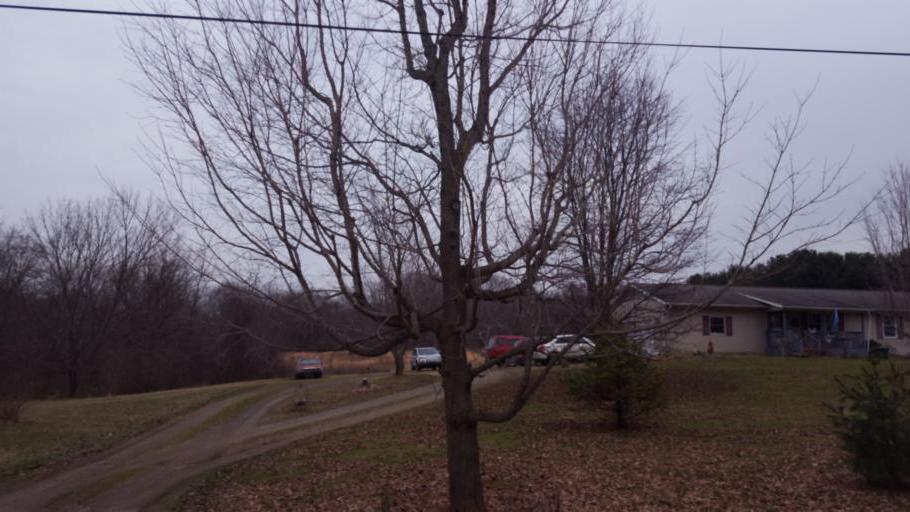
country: US
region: Ohio
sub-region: Morrow County
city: Mount Gilead
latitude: 40.6128
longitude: -82.8043
